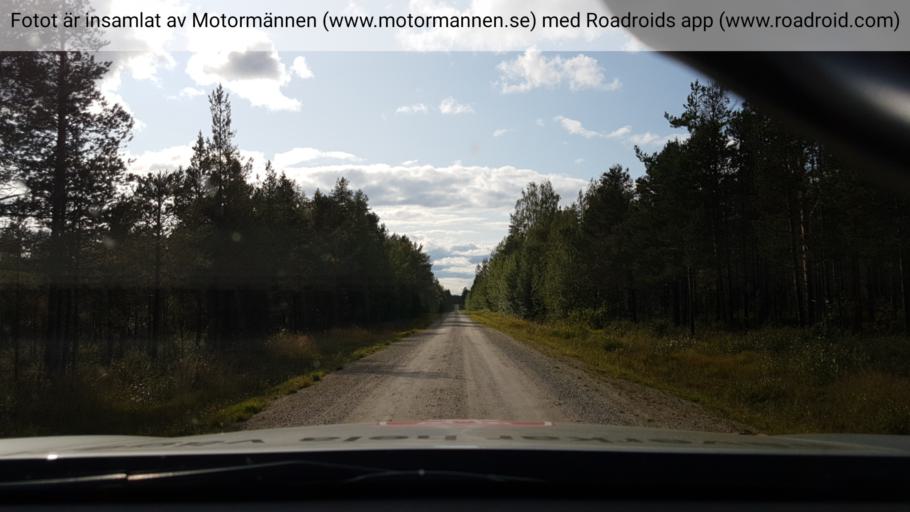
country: SE
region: Vaesterbotten
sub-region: Lycksele Kommun
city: Lycksele
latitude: 64.7292
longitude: 19.0454
